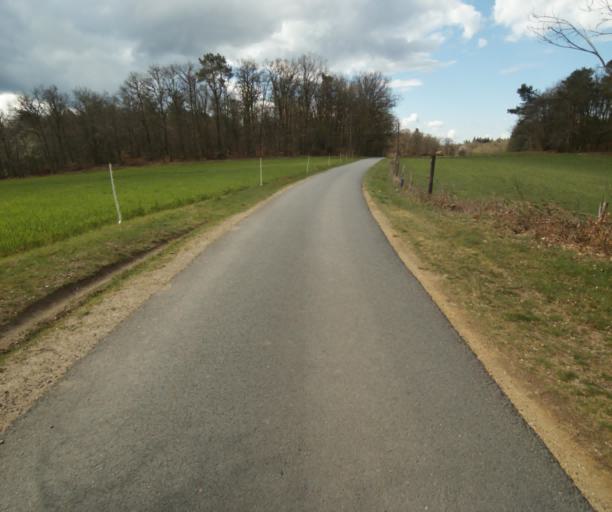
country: FR
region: Limousin
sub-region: Departement de la Correze
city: Correze
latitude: 45.2799
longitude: 1.9066
